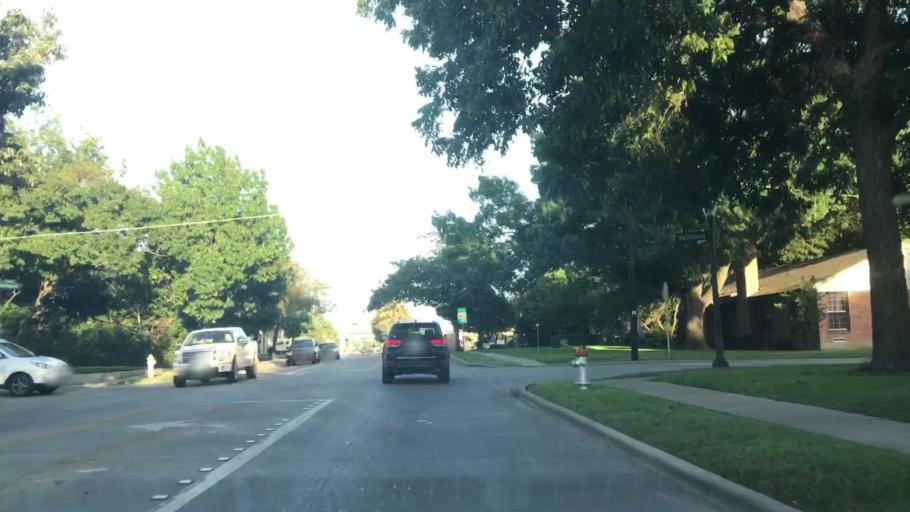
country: US
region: Texas
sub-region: Dallas County
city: Highland Park
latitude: 32.8511
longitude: -96.7738
